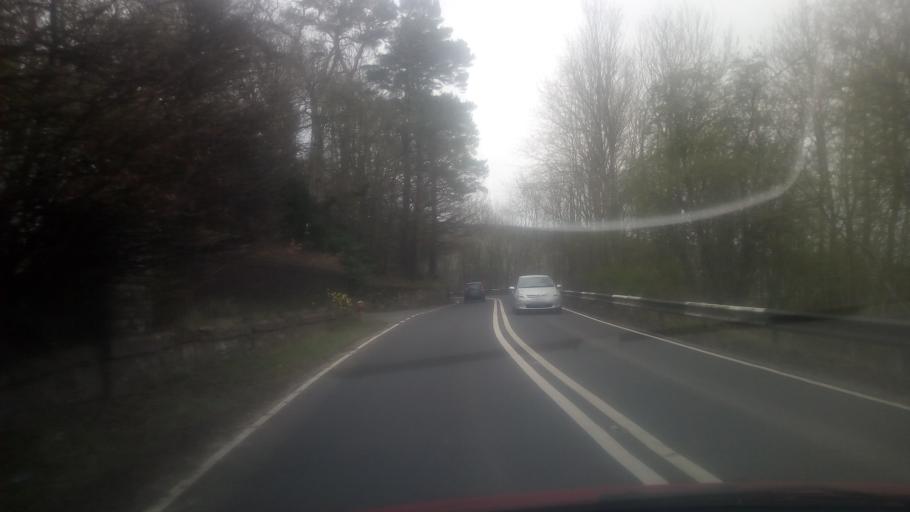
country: GB
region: Scotland
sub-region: The Scottish Borders
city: Galashiels
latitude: 55.6810
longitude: -2.8685
